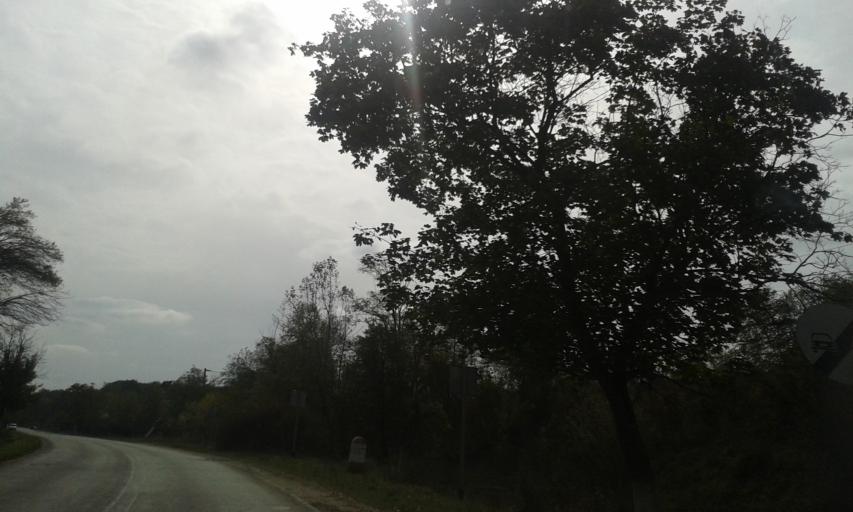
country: RO
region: Gorj
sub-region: Comuna Targu Carbunesti
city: Targu Carbunesti
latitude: 44.9717
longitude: 23.5026
